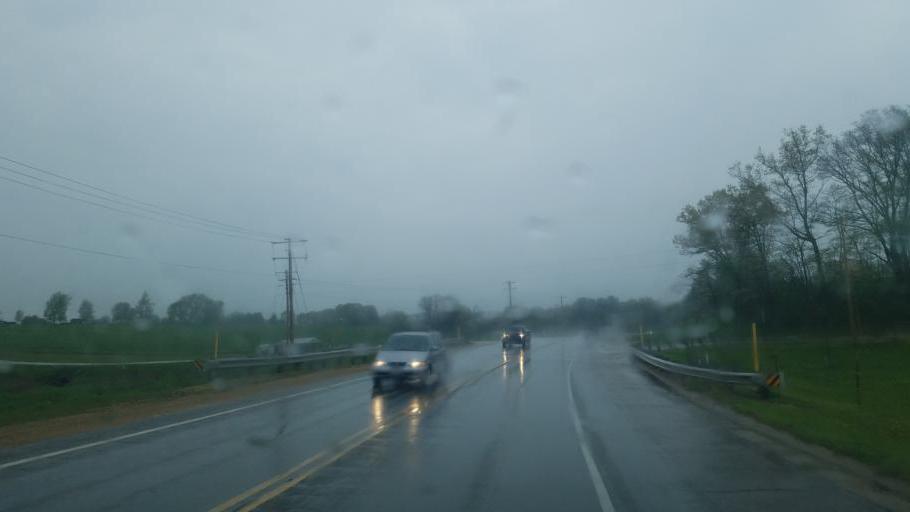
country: US
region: Wisconsin
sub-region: Sauk County
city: Reedsburg
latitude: 43.5688
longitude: -90.0996
